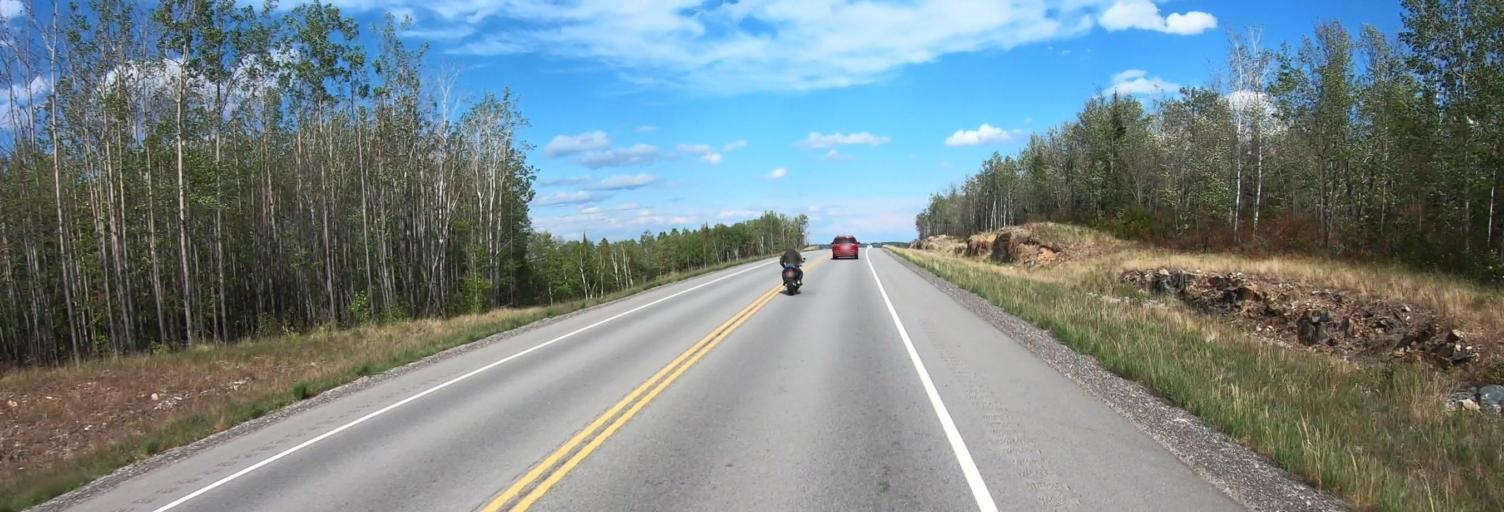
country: US
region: Minnesota
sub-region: Saint Louis County
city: Babbitt
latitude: 47.8428
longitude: -92.1440
